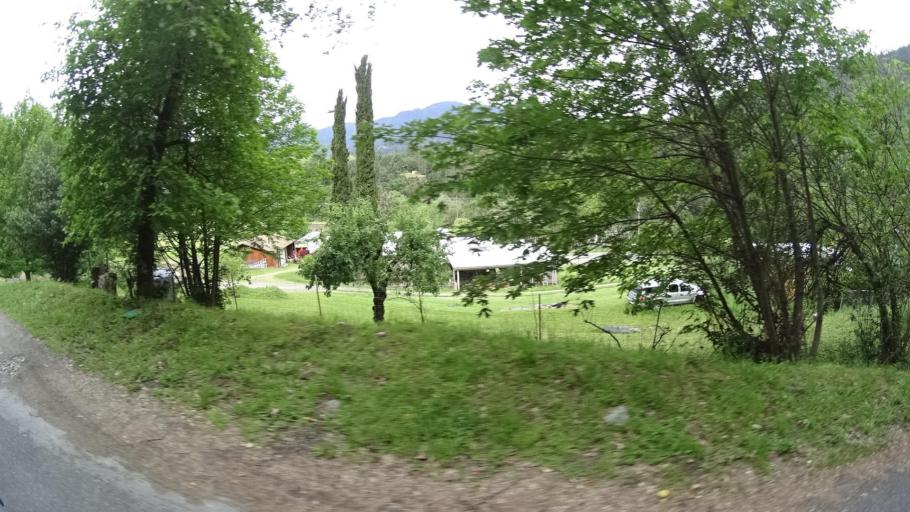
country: US
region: California
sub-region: Humboldt County
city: Willow Creek
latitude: 40.9439
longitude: -123.6114
